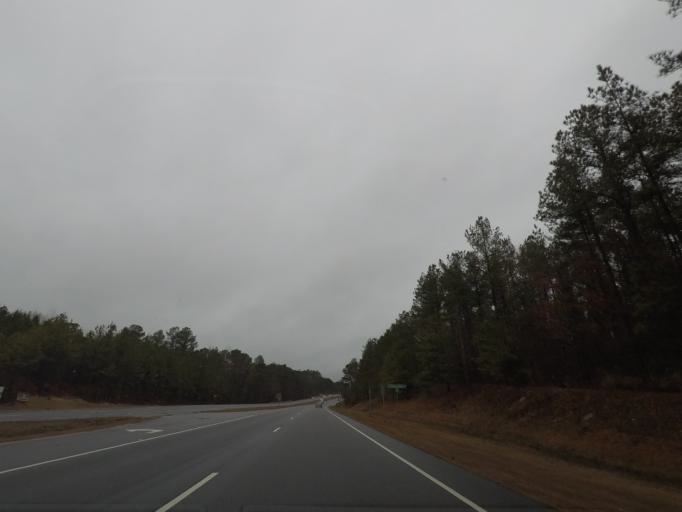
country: US
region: North Carolina
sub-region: Lee County
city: Broadway
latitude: 35.3258
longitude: -79.0929
